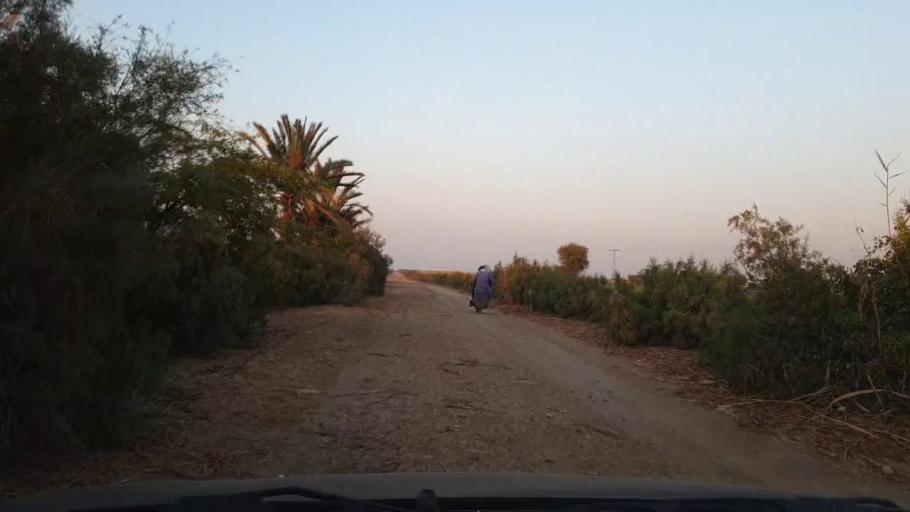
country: PK
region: Sindh
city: Jhol
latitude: 25.9225
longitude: 68.9640
